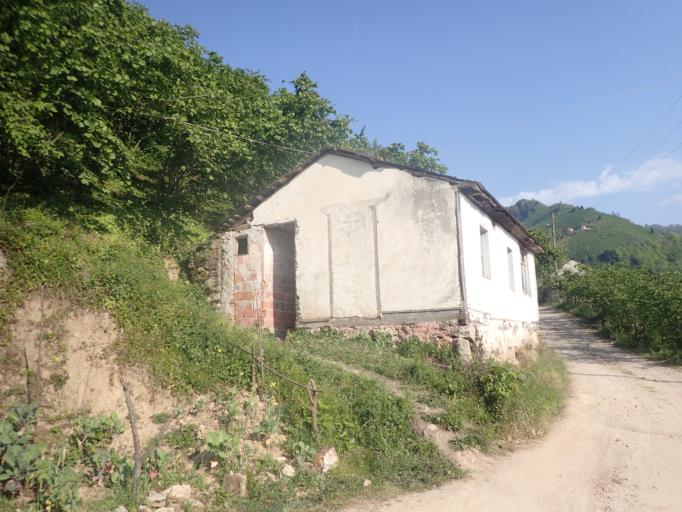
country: TR
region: Ordu
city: Kabaduz
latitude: 40.7917
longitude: 37.8867
